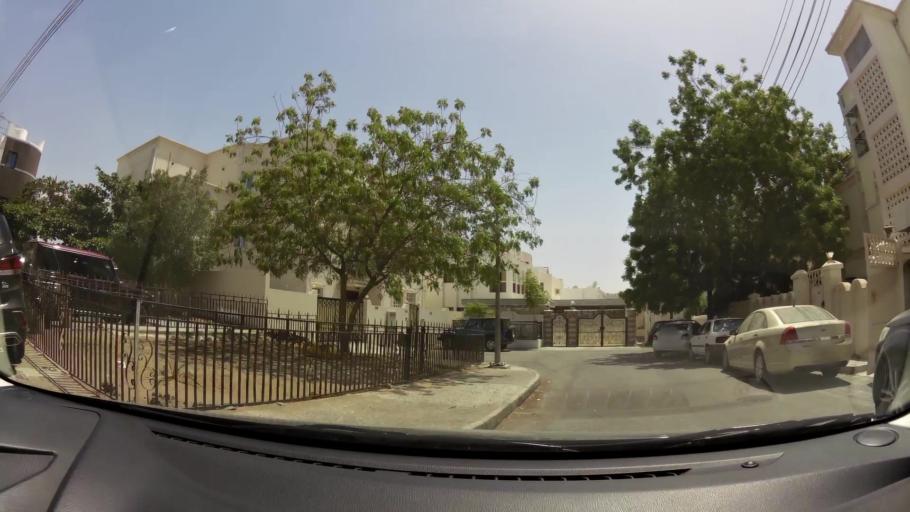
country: OM
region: Muhafazat Masqat
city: Muscat
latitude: 23.6191
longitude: 58.4976
